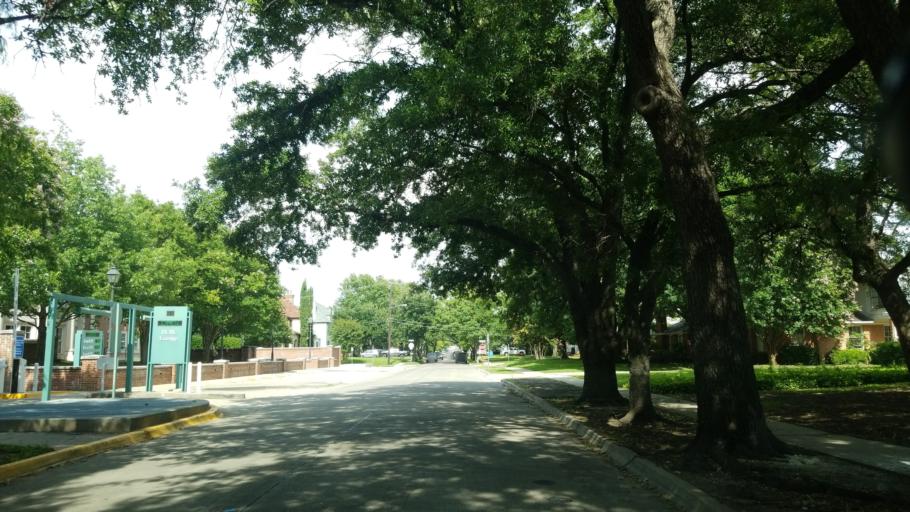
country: US
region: Texas
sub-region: Dallas County
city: University Park
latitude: 32.8644
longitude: -96.7996
